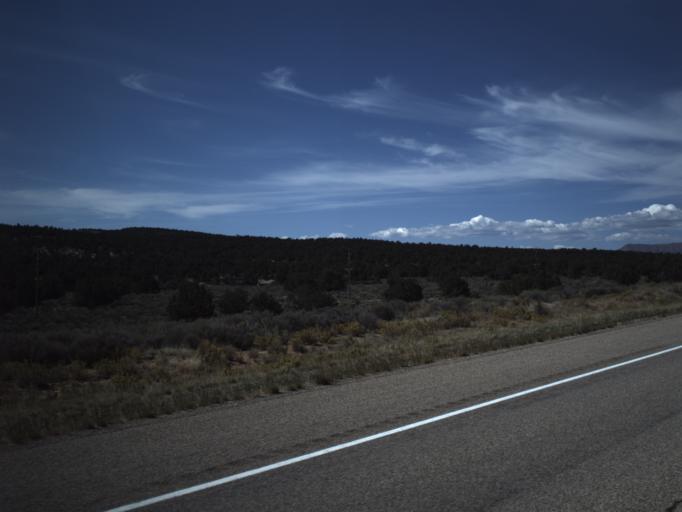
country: US
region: Utah
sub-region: Washington County
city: Ivins
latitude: 37.2746
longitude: -113.6463
